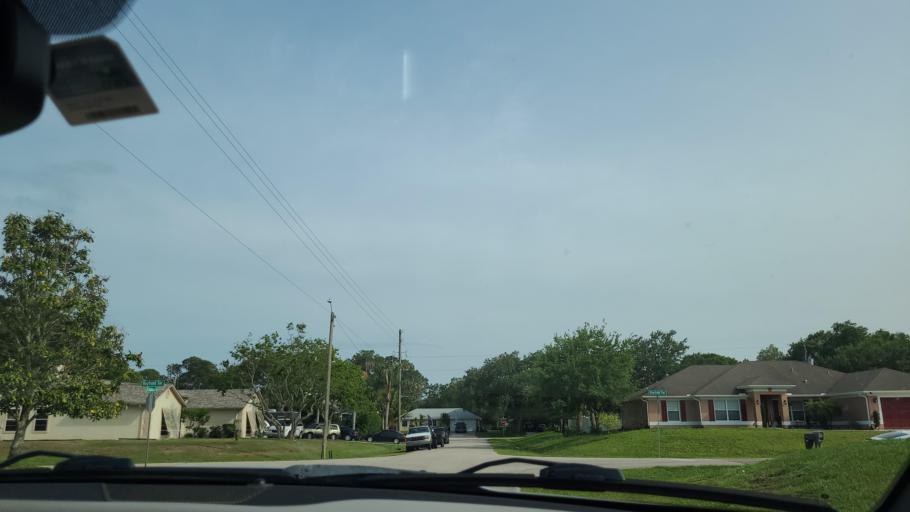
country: US
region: Florida
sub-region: Indian River County
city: Sebastian
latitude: 27.7706
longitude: -80.4906
